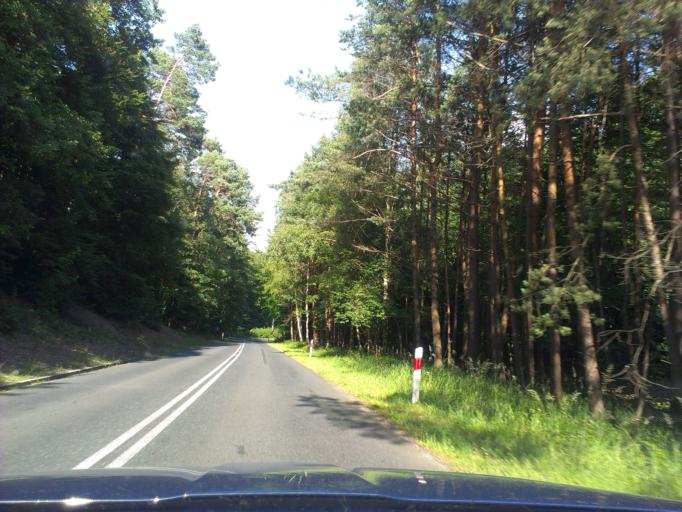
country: PL
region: West Pomeranian Voivodeship
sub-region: Powiat kamienski
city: Miedzyzdroje
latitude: 53.9647
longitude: 14.5417
